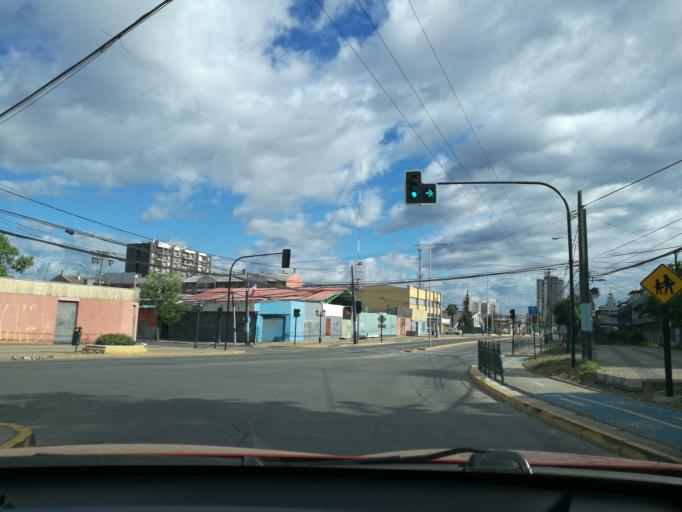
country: CL
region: O'Higgins
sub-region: Provincia de Cachapoal
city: Rancagua
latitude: -34.1761
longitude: -70.7361
